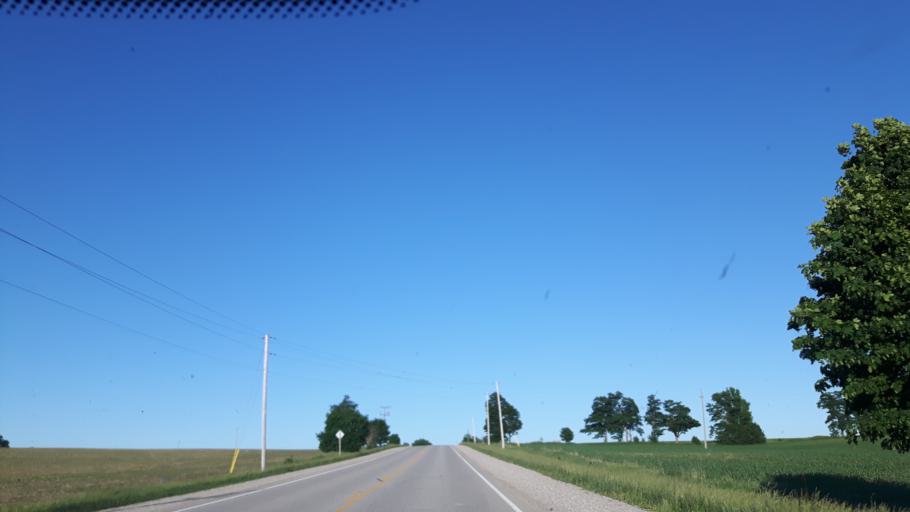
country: CA
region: Ontario
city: Goderich
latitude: 43.6427
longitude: -81.6212
